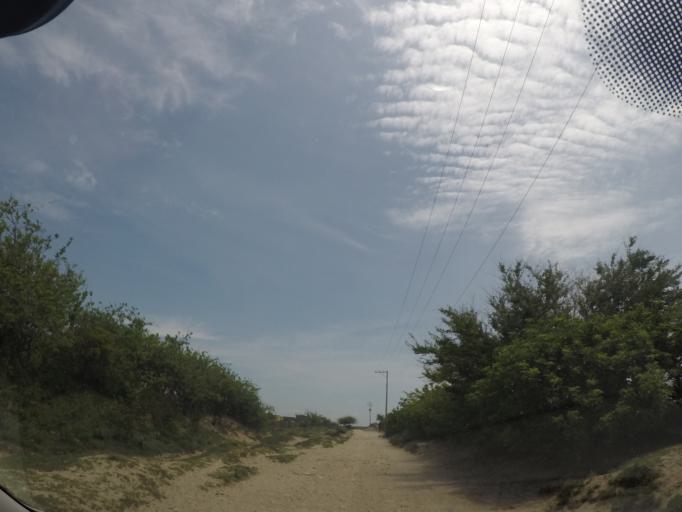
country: MX
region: Oaxaca
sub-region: San Mateo del Mar
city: Colonia Juarez
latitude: 16.2120
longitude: -95.0358
